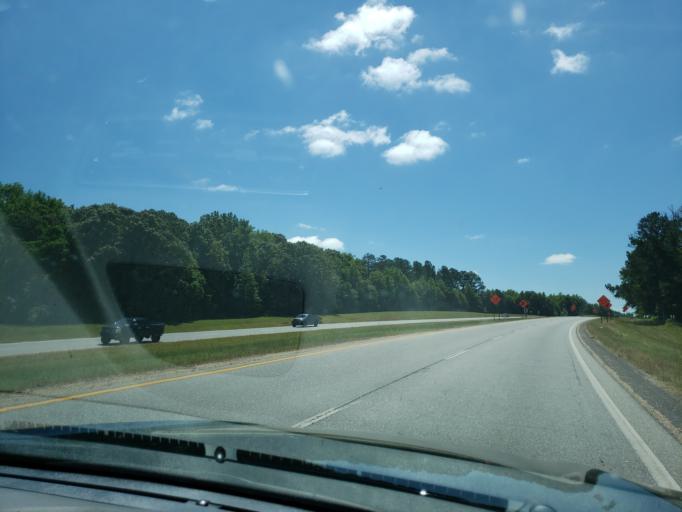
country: US
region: Alabama
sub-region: Lee County
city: Auburn
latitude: 32.6884
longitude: -85.4981
